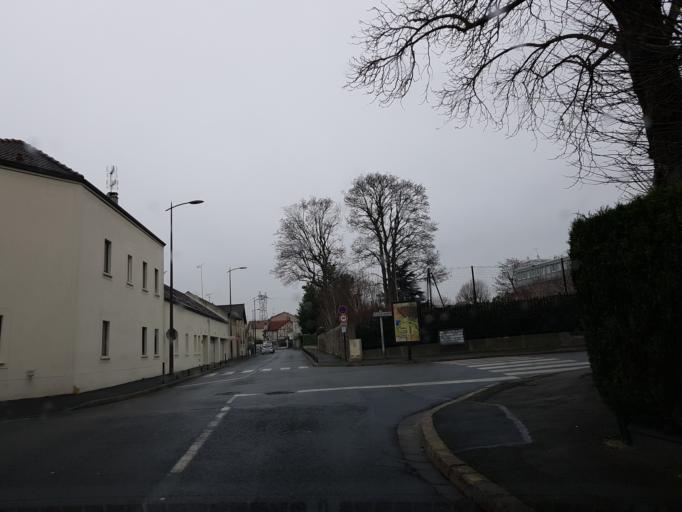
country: FR
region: Ile-de-France
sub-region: Departement du Val-de-Marne
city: Thiais
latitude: 48.7631
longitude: 2.3941
